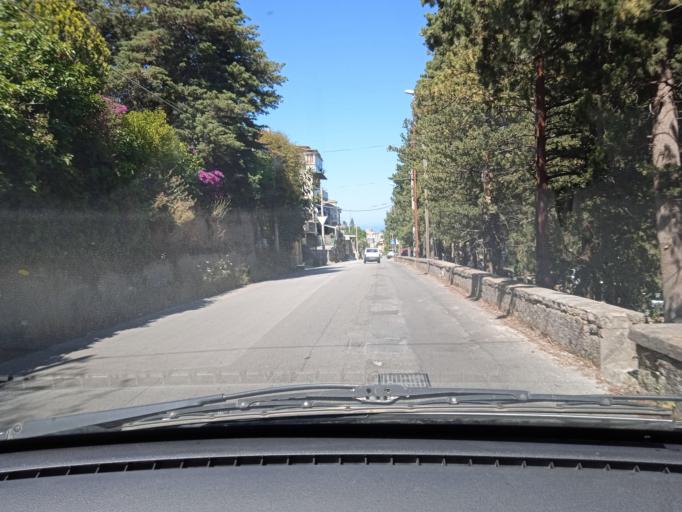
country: IT
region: Sicily
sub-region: Palermo
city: Cannizzaro-Favara
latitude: 38.0729
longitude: 13.2730
